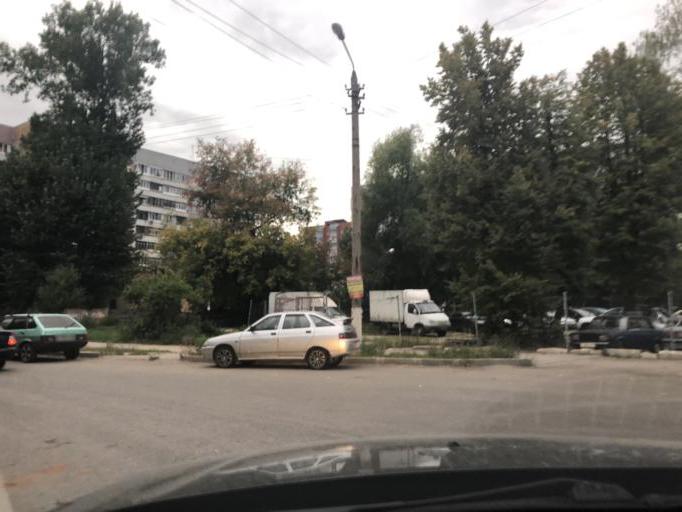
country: RU
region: Tula
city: Tula
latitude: 54.2093
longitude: 37.6269
